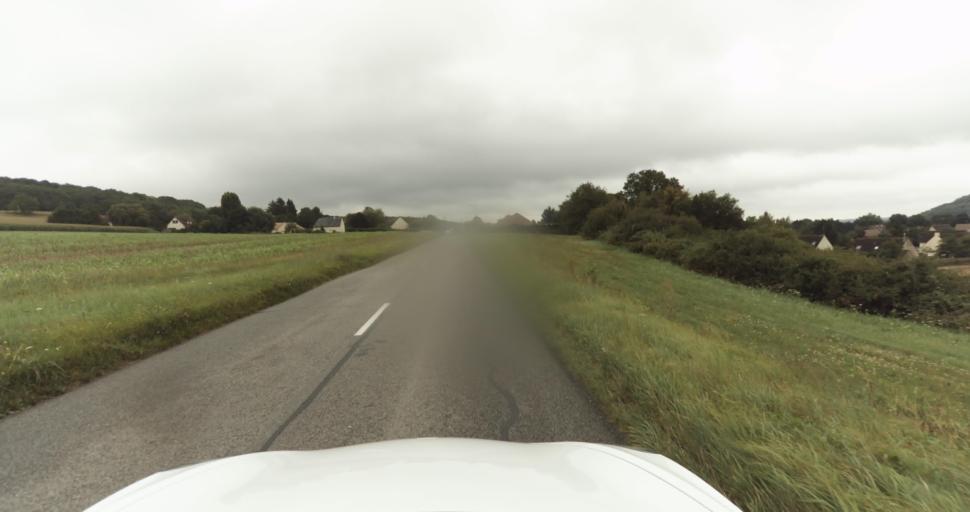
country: FR
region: Haute-Normandie
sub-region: Departement de l'Eure
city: Normanville
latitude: 49.0726
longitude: 1.1690
